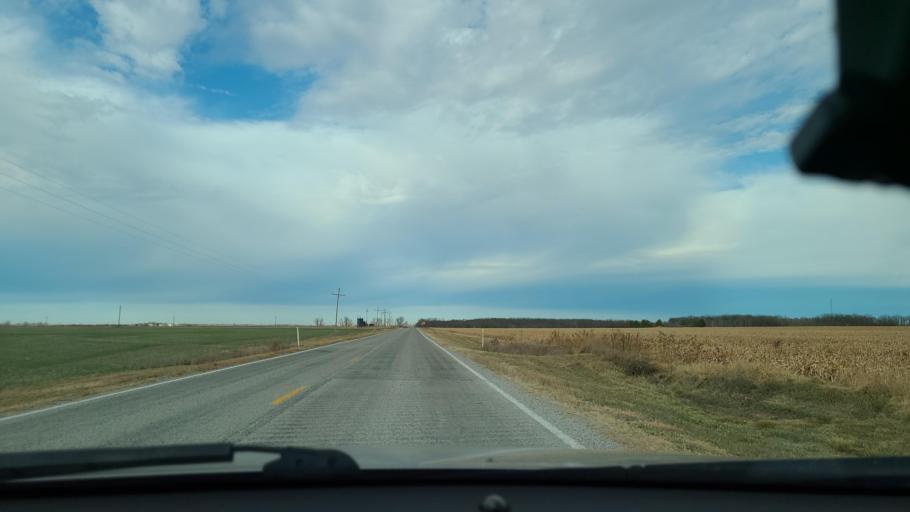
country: US
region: Kansas
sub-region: McPherson County
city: Inman
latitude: 38.3731
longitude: -97.9245
